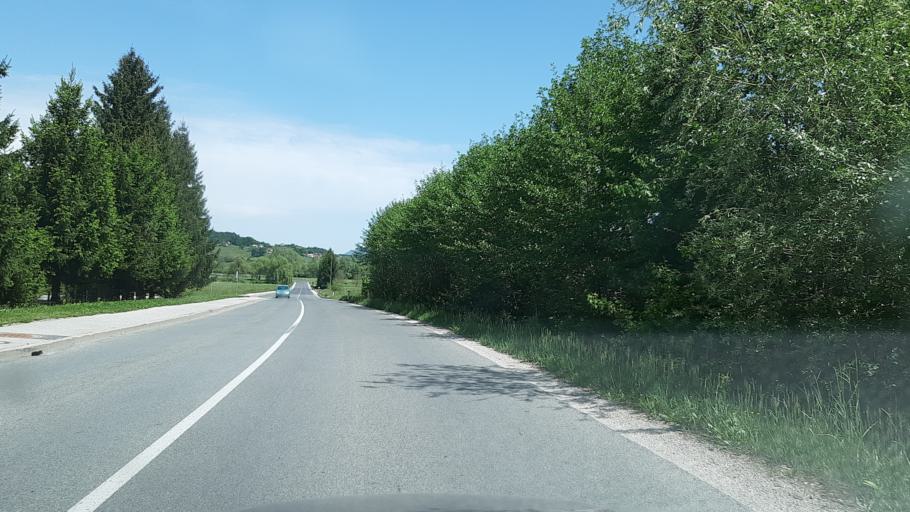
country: SI
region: Sentjur pri Celju
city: Sentjur
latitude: 46.2080
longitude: 15.4036
